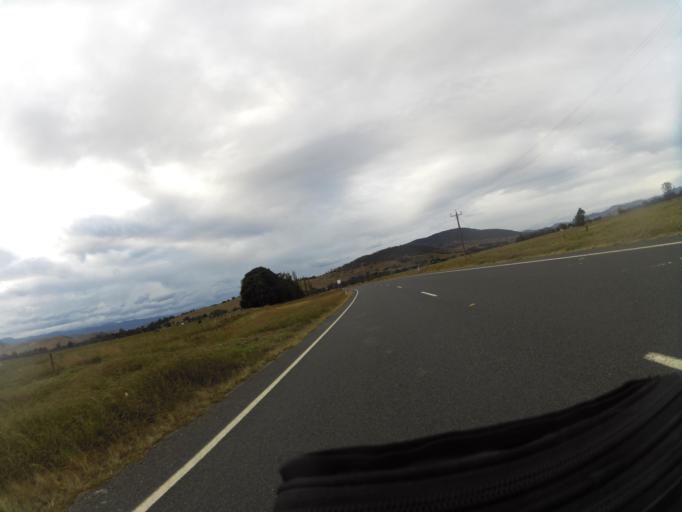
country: AU
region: New South Wales
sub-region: Snowy River
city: Jindabyne
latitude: -36.1150
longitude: 147.9792
